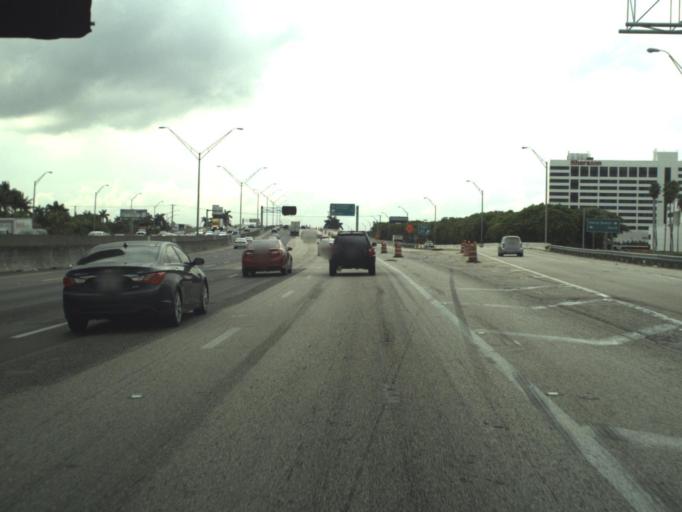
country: US
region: Florida
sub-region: Broward County
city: Dania Beach
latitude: 26.0577
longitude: -80.1624
